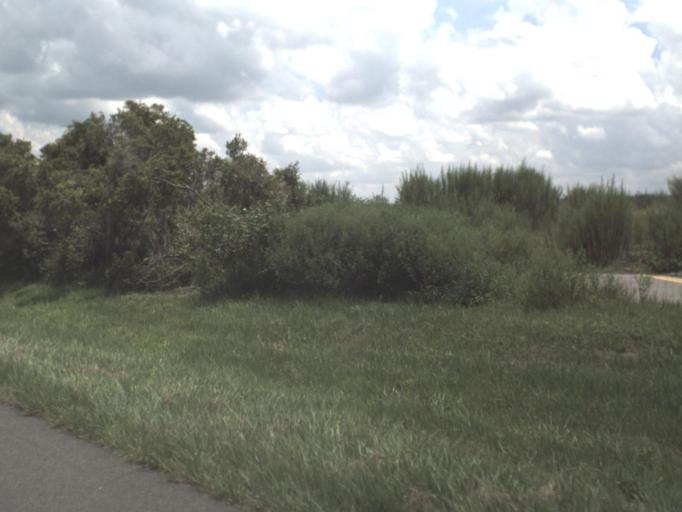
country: US
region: Florida
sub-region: Hillsborough County
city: Boyette
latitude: 27.7045
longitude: -82.1140
